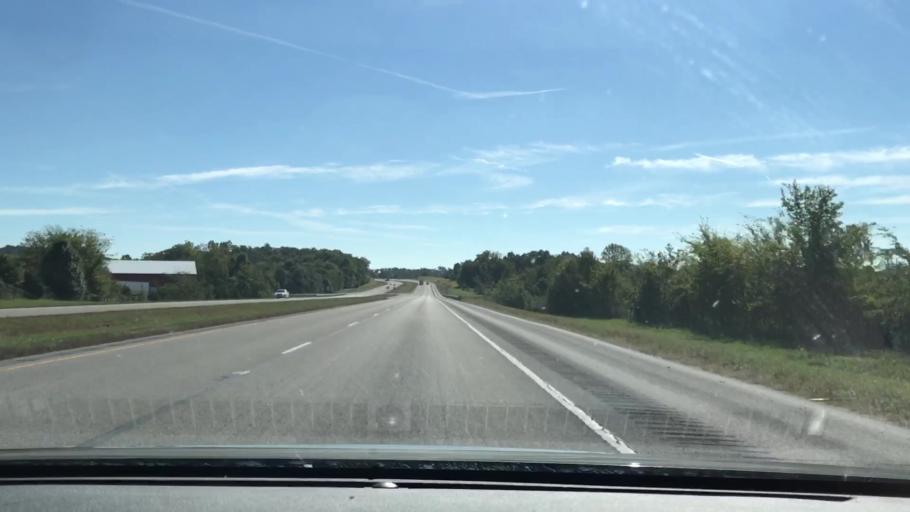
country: US
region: Kentucky
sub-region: Todd County
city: Elkton
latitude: 36.8316
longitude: -87.2294
